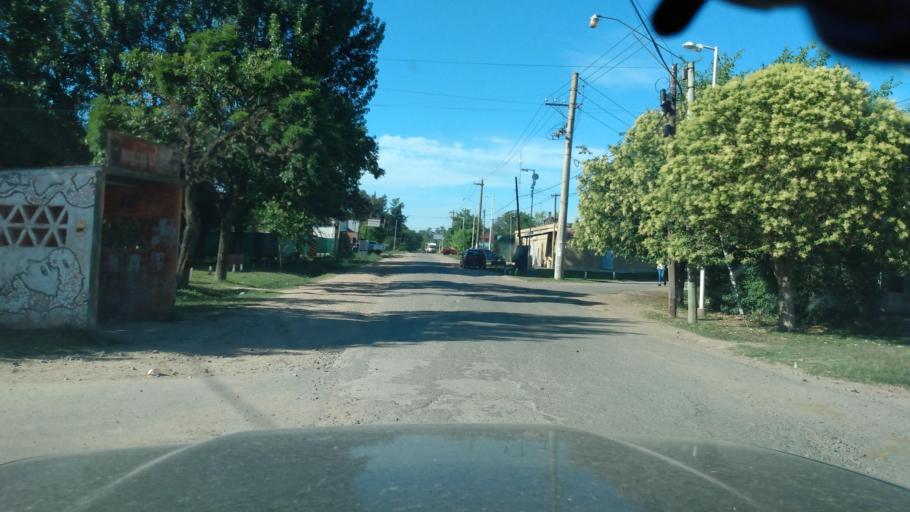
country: AR
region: Buenos Aires
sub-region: Partido de Lujan
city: Lujan
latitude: -34.5847
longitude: -59.0576
